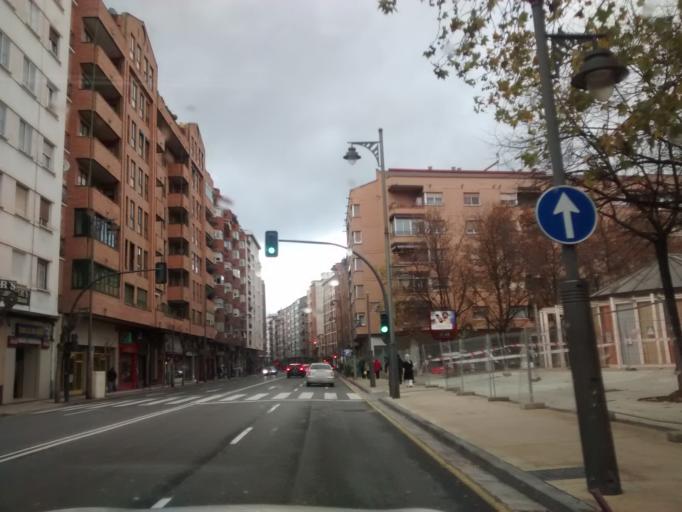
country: ES
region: La Rioja
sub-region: Provincia de La Rioja
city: Logrono
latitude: 42.4613
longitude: -2.4546
